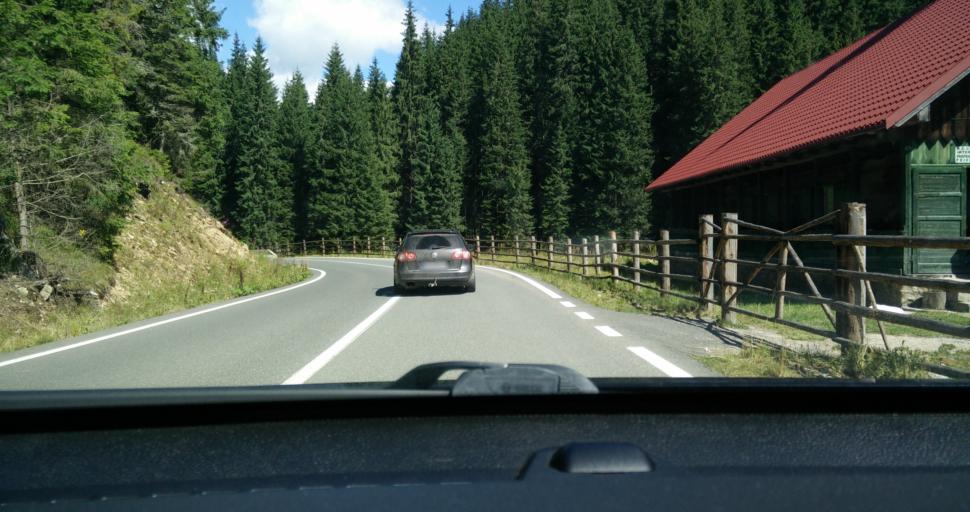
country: RO
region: Hunedoara
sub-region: Oras Petrila
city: Petrila
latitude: 45.5150
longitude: 23.6514
